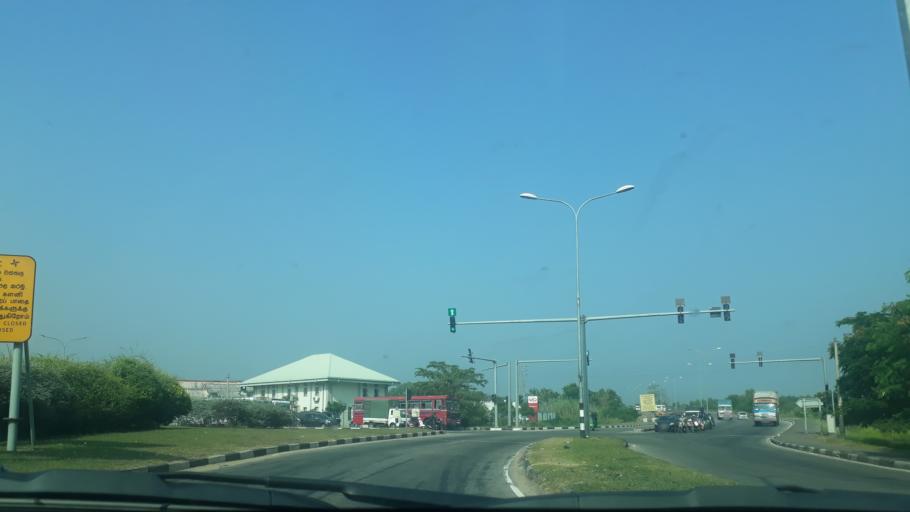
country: LK
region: Western
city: Wattala
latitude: 6.9678
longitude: 79.9021
